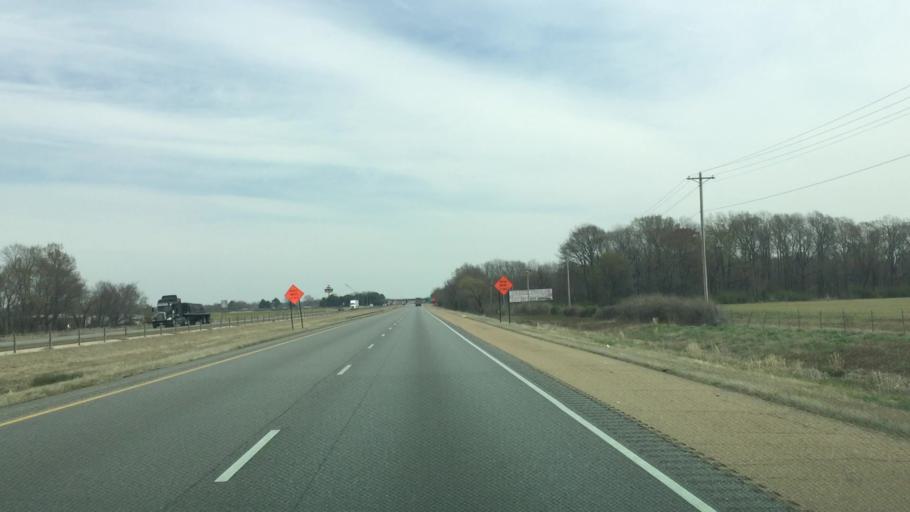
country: US
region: Arkansas
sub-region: Saint Francis County
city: Forrest City
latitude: 34.9787
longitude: -90.9166
